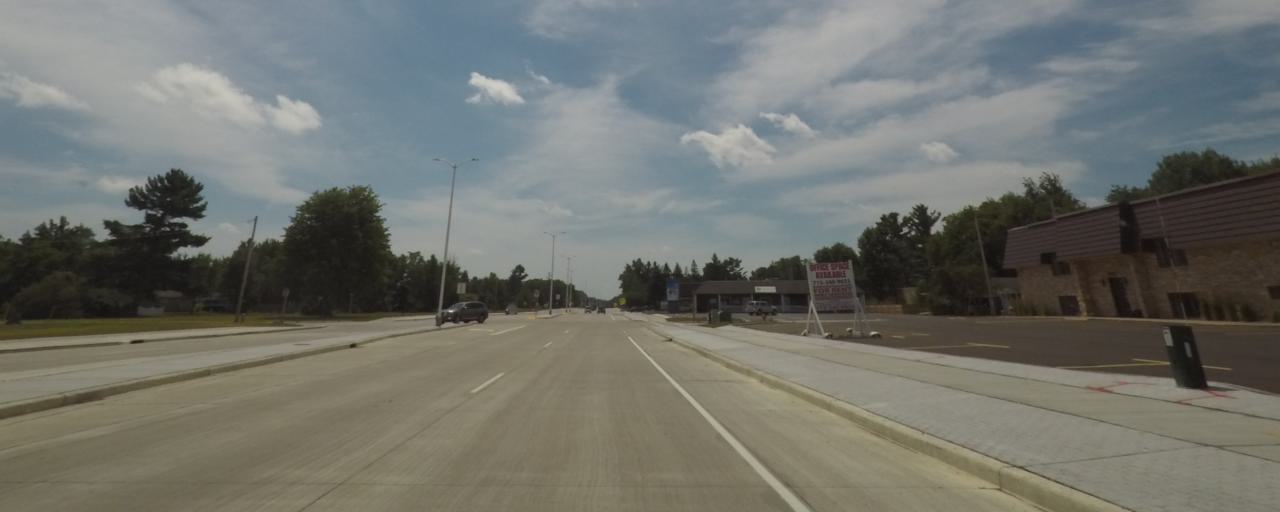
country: US
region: Wisconsin
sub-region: Portage County
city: Whiting
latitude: 44.4887
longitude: -89.5513
